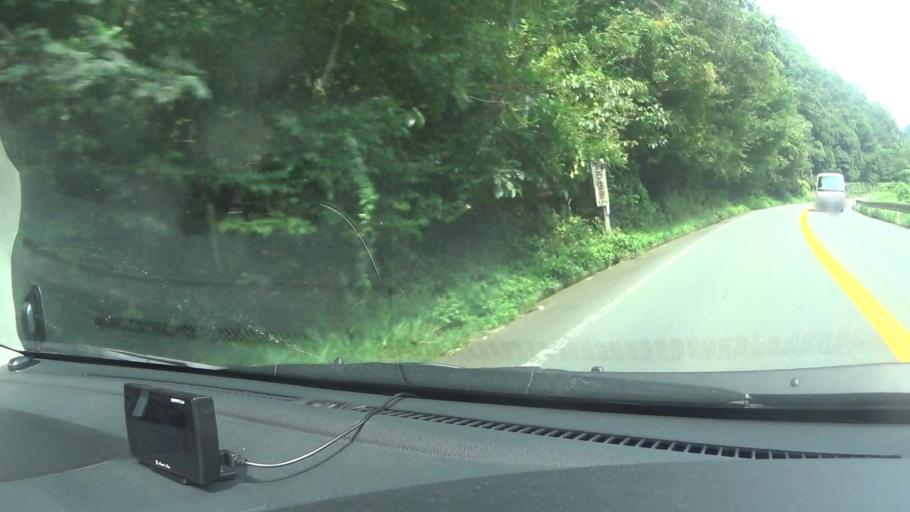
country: JP
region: Hyogo
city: Sasayama
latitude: 35.1501
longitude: 135.3548
